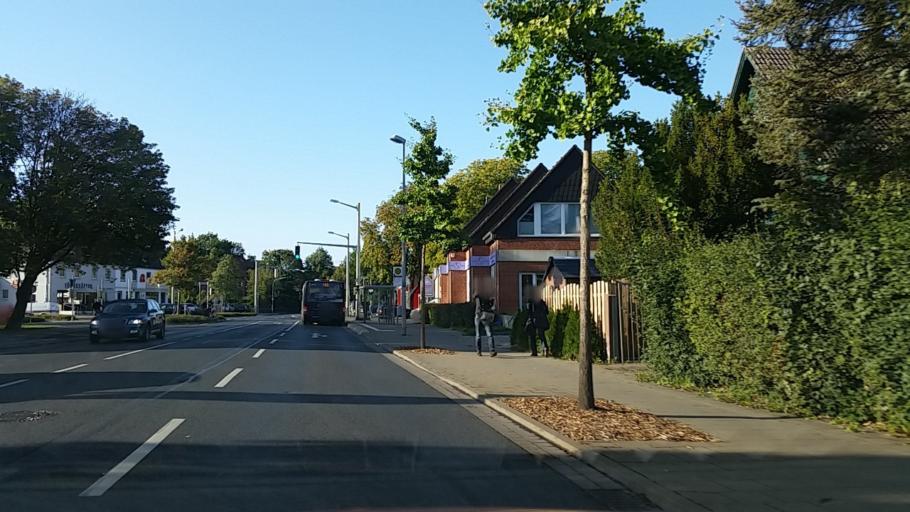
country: DE
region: Lower Saxony
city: Braunschweig
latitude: 52.2899
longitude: 10.5615
